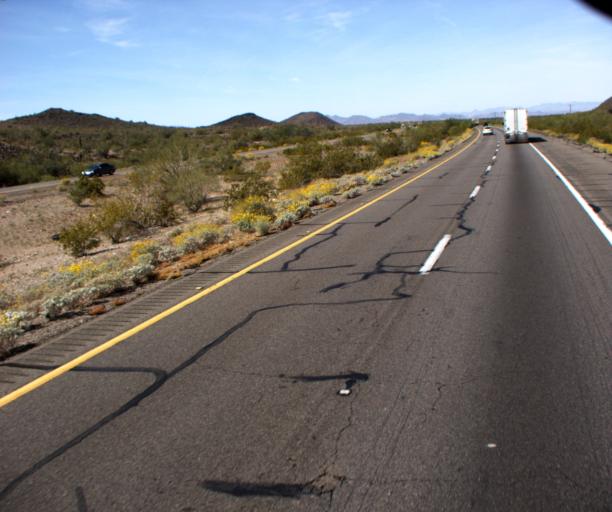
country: US
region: Arizona
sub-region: La Paz County
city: Quartzsite
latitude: 33.6772
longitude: -114.0569
